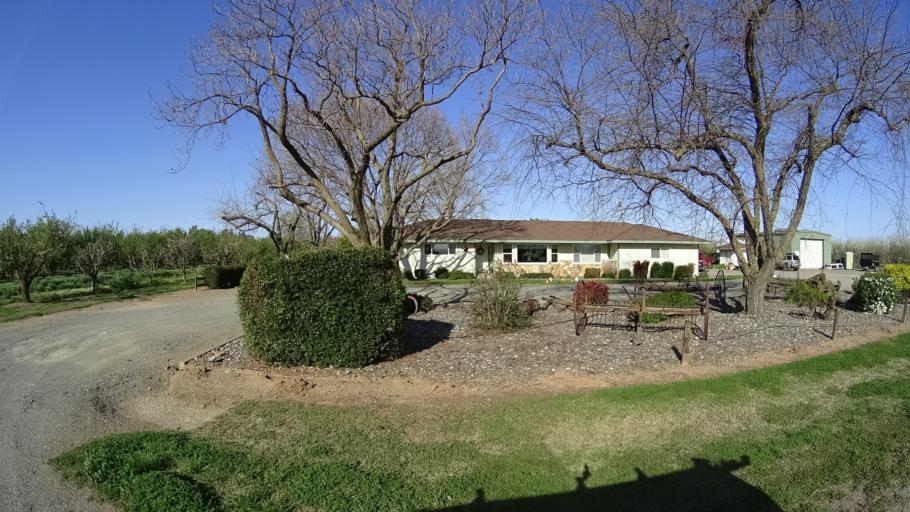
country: US
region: California
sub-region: Glenn County
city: Orland
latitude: 39.7649
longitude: -122.1228
